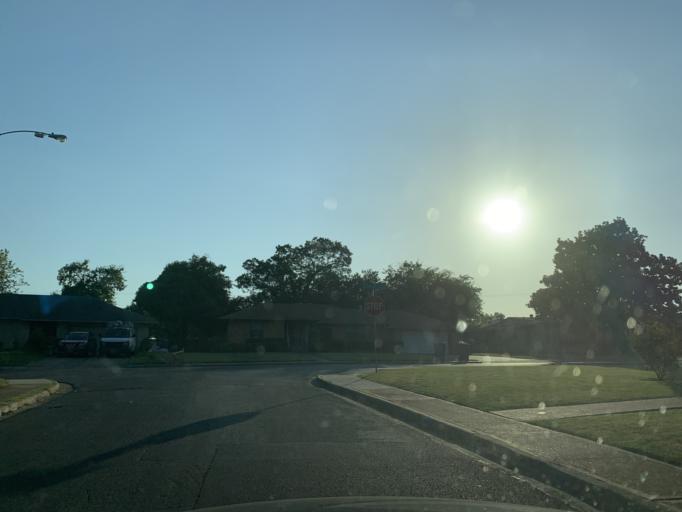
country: US
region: Texas
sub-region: Dallas County
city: Dallas
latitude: 32.7117
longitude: -96.8031
